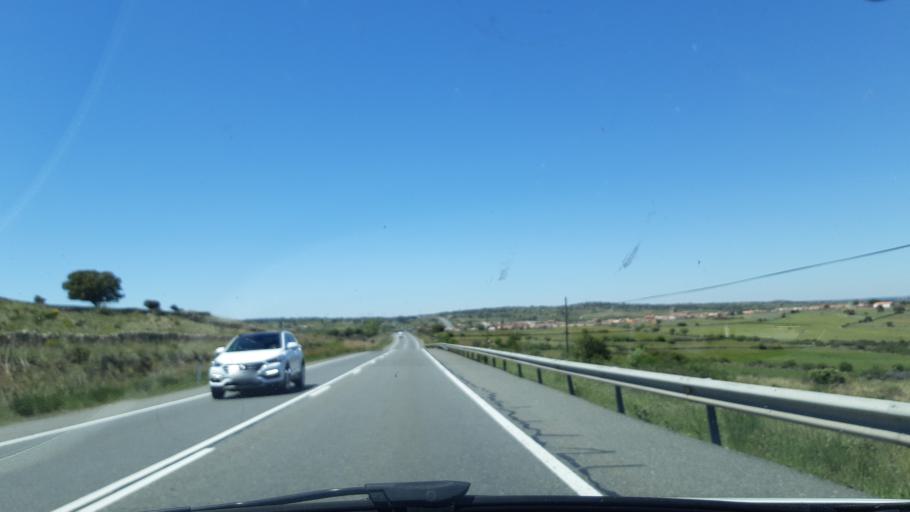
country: ES
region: Castille and Leon
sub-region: Provincia de Segovia
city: Vegas de Matute
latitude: 40.7538
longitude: -4.3154
